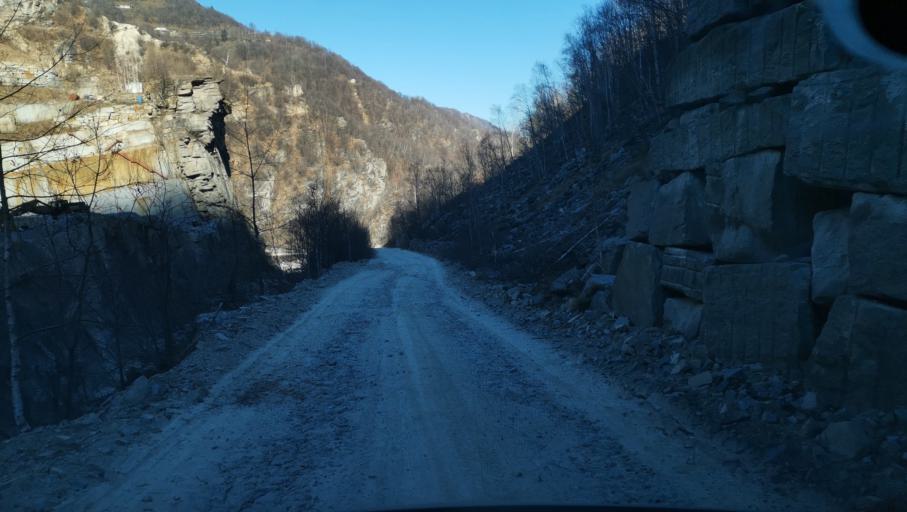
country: IT
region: Piedmont
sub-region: Provincia di Torino
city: Rora
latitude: 44.7632
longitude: 7.2006
